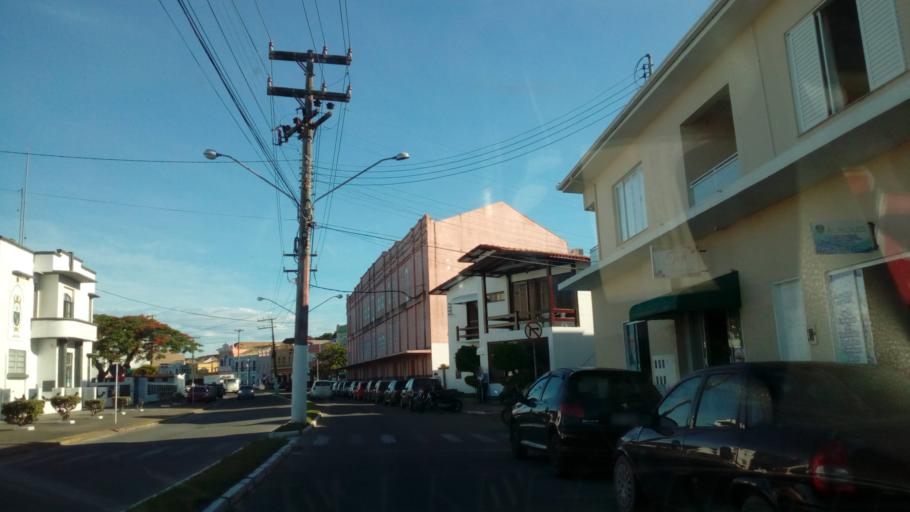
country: BR
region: Santa Catarina
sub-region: Laguna
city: Laguna
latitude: -28.4858
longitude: -48.7828
